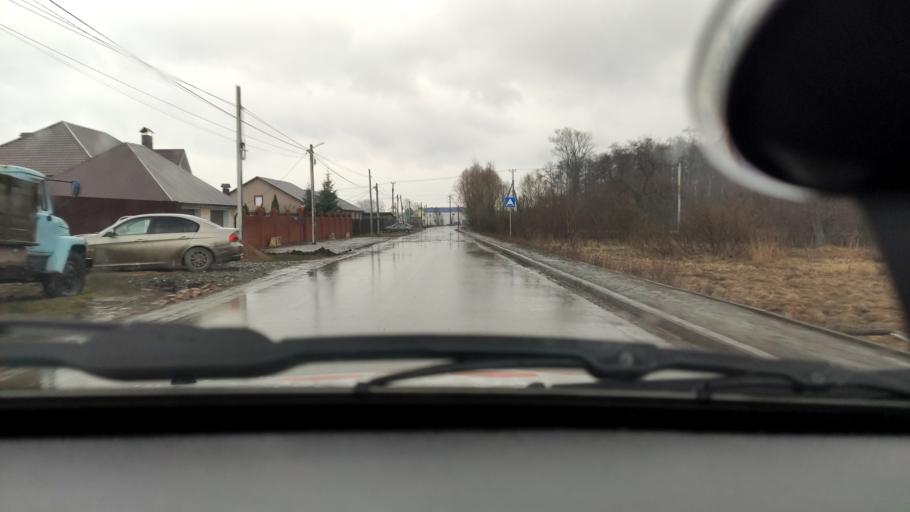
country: RU
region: Bashkortostan
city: Mikhaylovka
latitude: 54.7844
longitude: 55.8168
